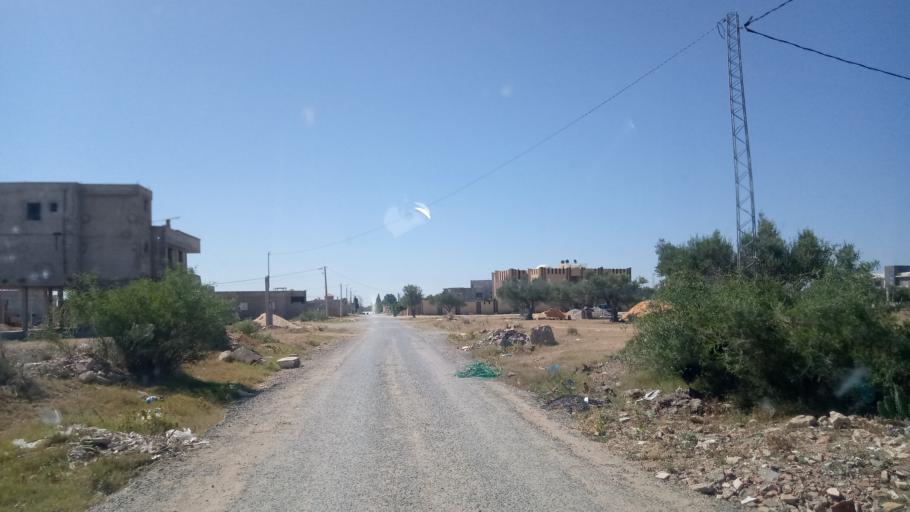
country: TN
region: Al Qayrawan
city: Sbikha
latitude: 36.1263
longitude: 10.0859
